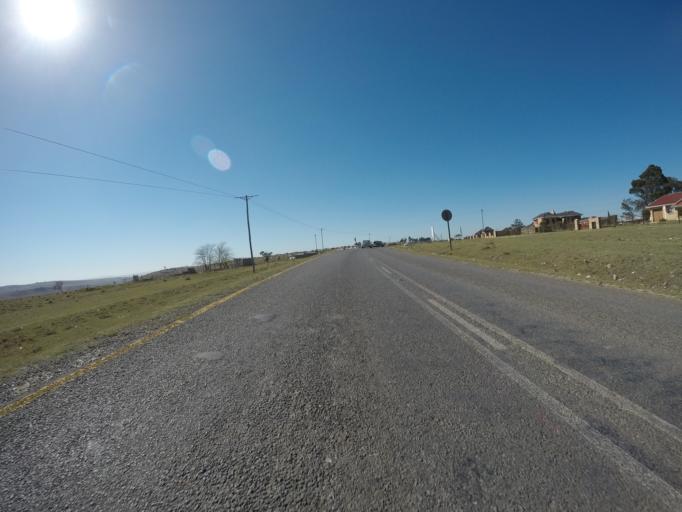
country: ZA
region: Eastern Cape
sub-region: OR Tambo District Municipality
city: Mthatha
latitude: -31.7829
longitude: 28.7398
